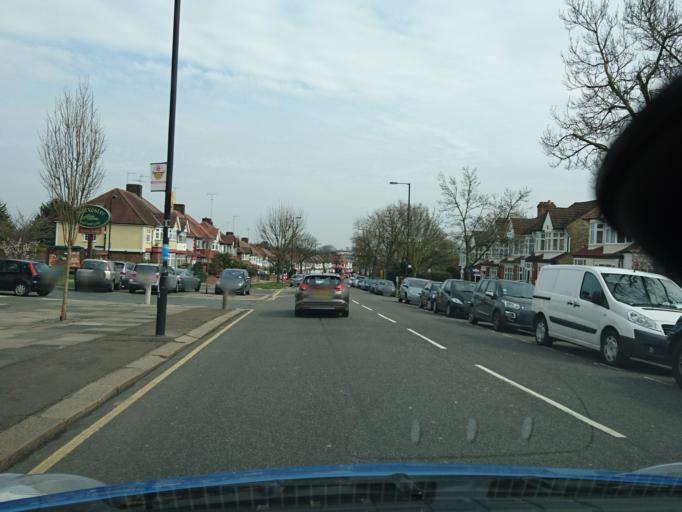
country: GB
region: England
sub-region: Greater London
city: Wood Green
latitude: 51.6160
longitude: -0.1324
